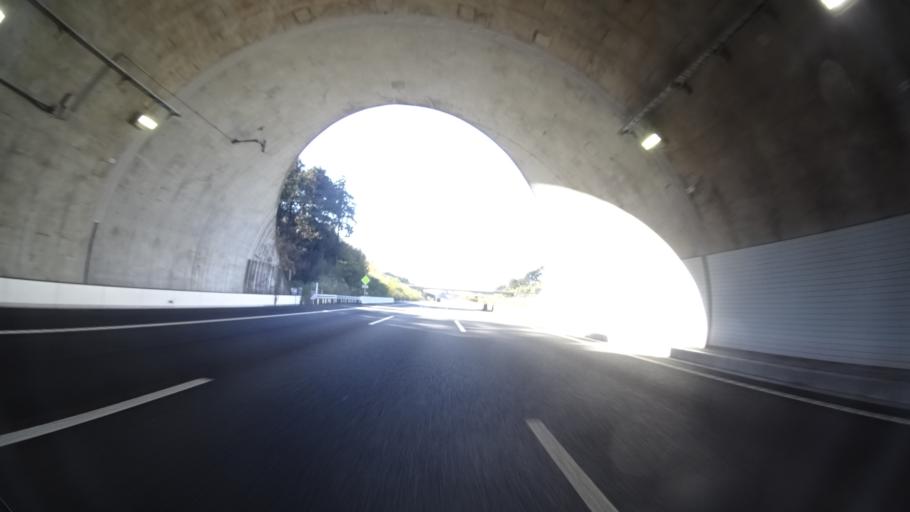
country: JP
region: Shizuoka
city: Mori
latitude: 34.8373
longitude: 137.9806
